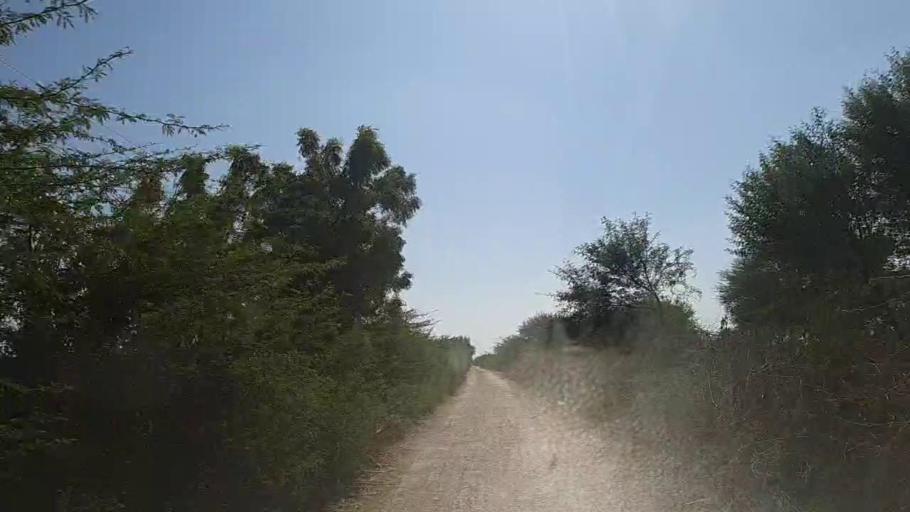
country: PK
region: Sindh
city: Naukot
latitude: 25.0017
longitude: 69.3733
